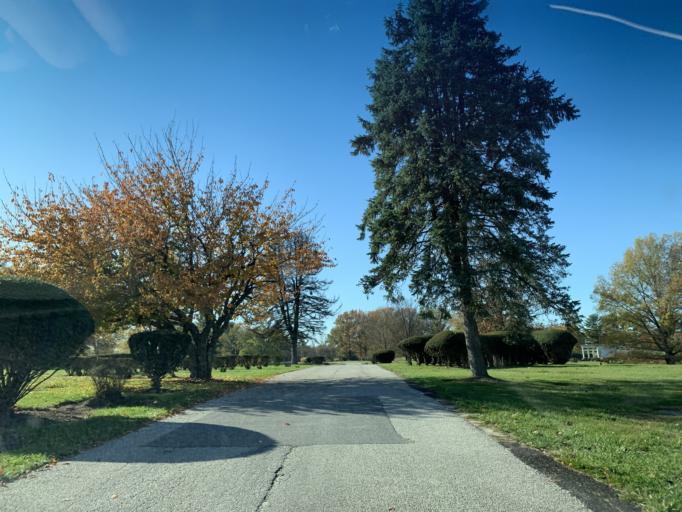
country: US
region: Maryland
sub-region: Baltimore County
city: Timonium
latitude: 39.4563
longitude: -76.6180
